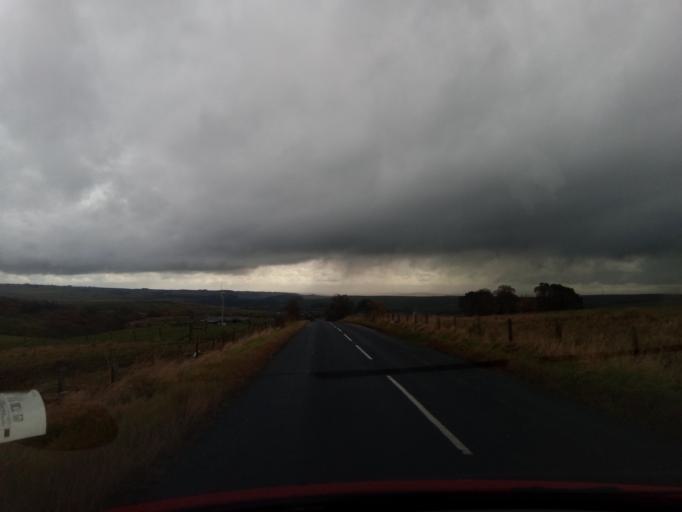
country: GB
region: England
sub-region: Northumberland
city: Corsenside
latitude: 55.1608
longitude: -2.2640
